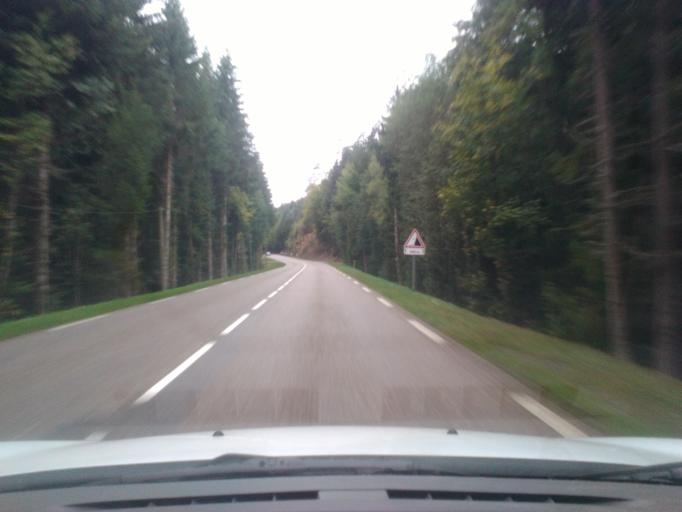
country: FR
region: Lorraine
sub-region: Departement des Vosges
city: Jeanmenil
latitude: 48.3221
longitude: 6.7514
